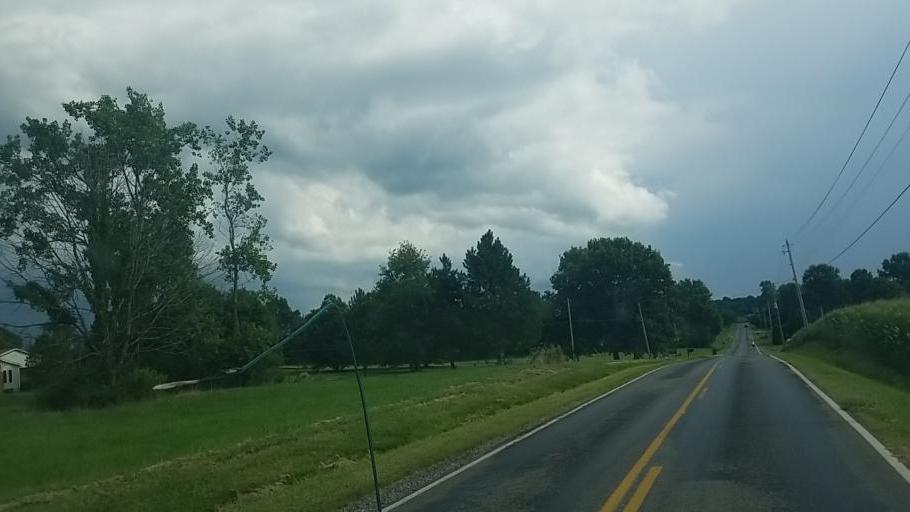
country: US
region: Ohio
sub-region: Wayne County
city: Creston
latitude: 41.0081
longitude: -81.9110
